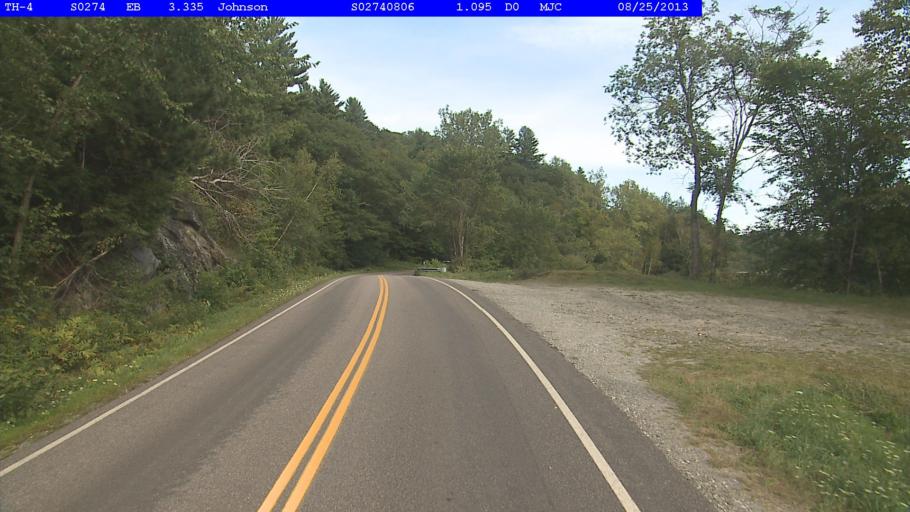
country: US
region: Vermont
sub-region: Lamoille County
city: Johnson
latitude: 44.6527
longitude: -72.7304
